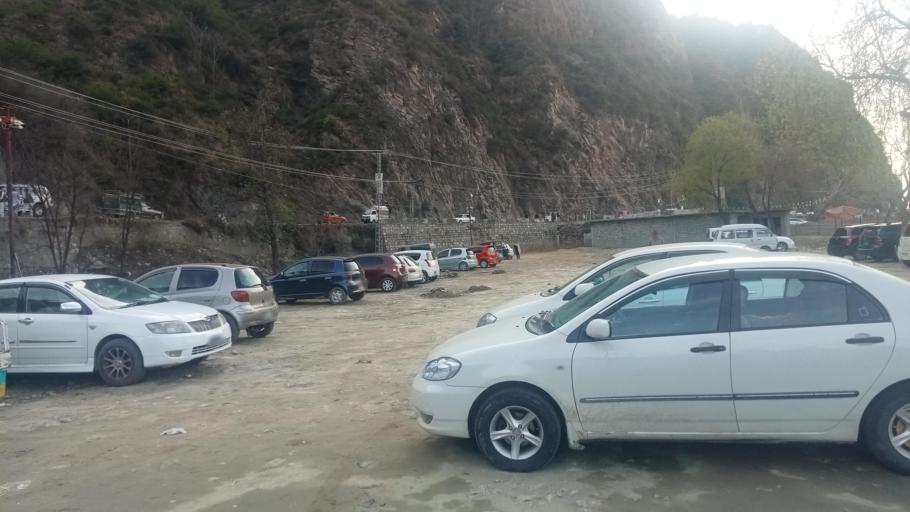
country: PK
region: Khyber Pakhtunkhwa
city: Mingora
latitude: 34.7917
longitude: 72.3914
